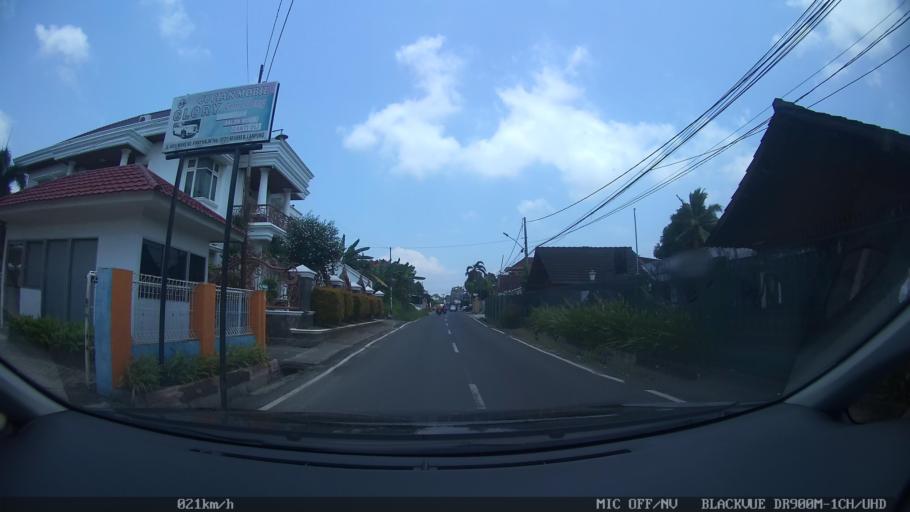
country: ID
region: Lampung
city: Kedaton
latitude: -5.3748
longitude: 105.2727
